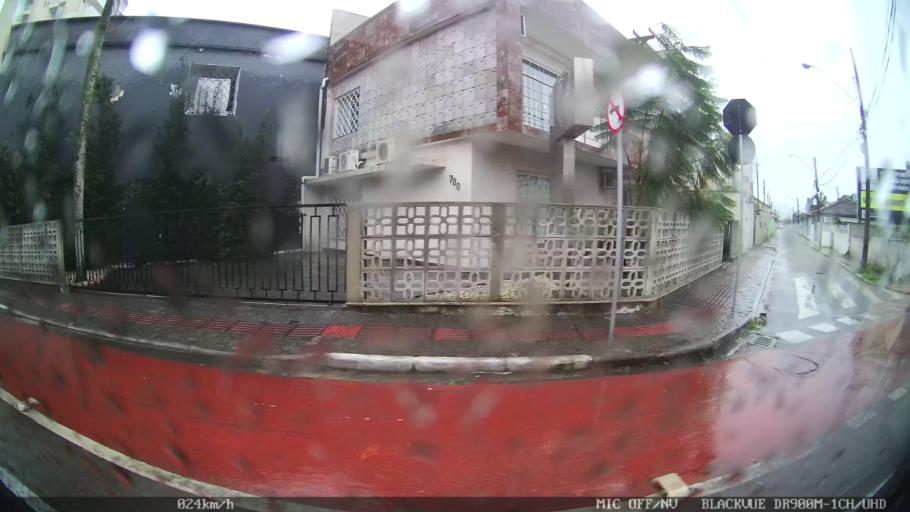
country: BR
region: Santa Catarina
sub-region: Itajai
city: Itajai
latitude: -26.9097
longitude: -48.6686
